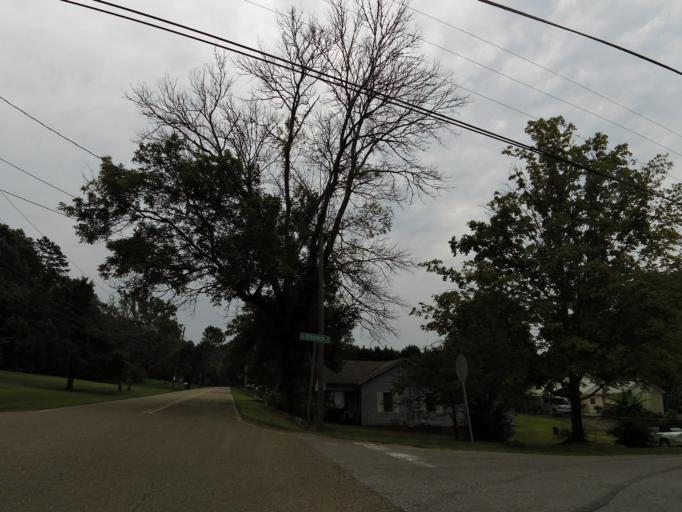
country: US
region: Tennessee
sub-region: Sevier County
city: Seymour
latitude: 35.9246
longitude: -83.7962
